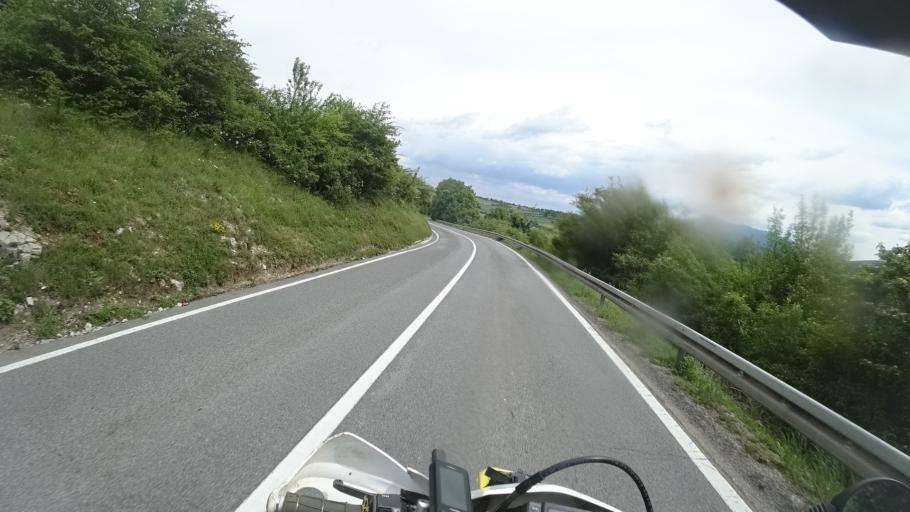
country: BA
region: Federation of Bosnia and Herzegovina
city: Izacic
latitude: 44.9203
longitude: 15.7058
